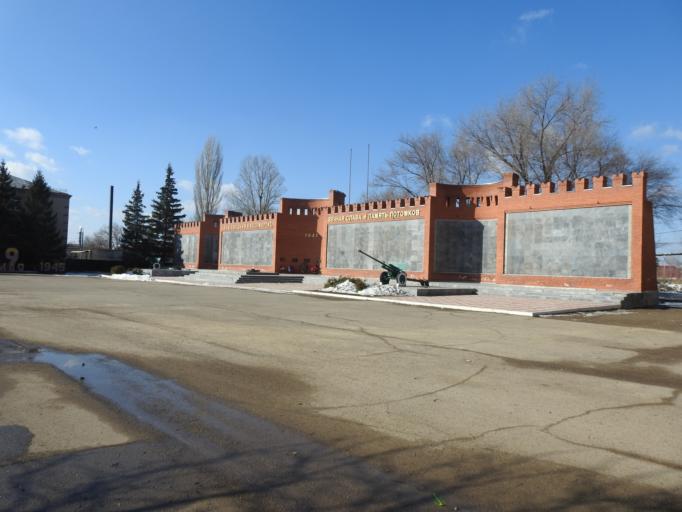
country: RU
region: Saratov
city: Yershov
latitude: 51.3502
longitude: 48.2658
